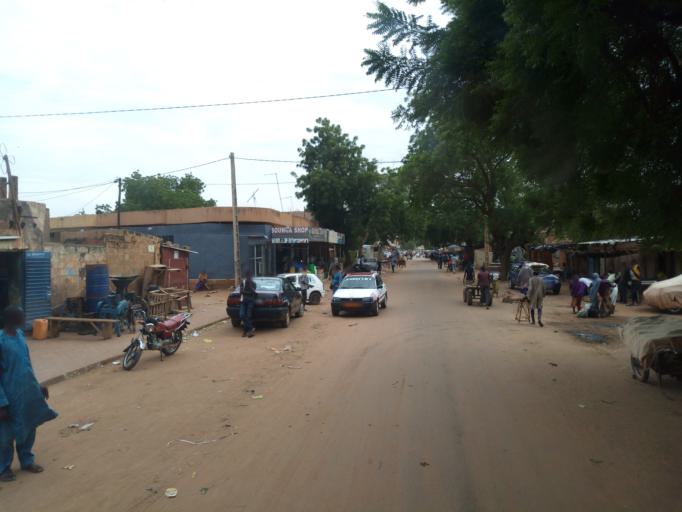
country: NE
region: Niamey
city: Niamey
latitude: 13.5190
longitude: 2.1147
